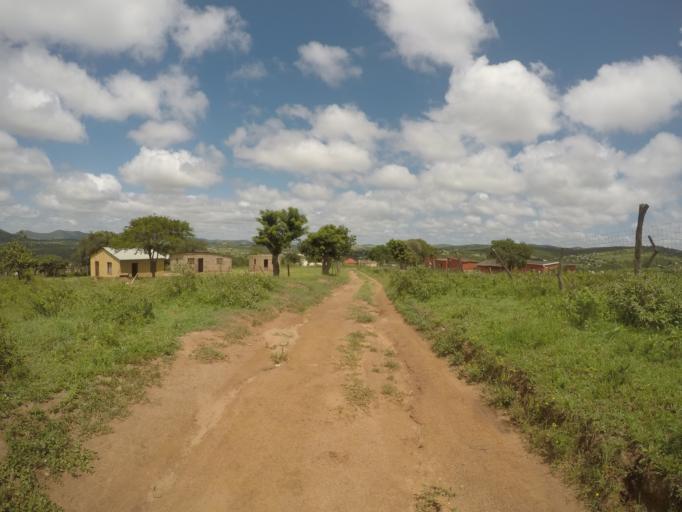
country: ZA
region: KwaZulu-Natal
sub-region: uThungulu District Municipality
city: Empangeni
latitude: -28.5785
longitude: 31.8420
